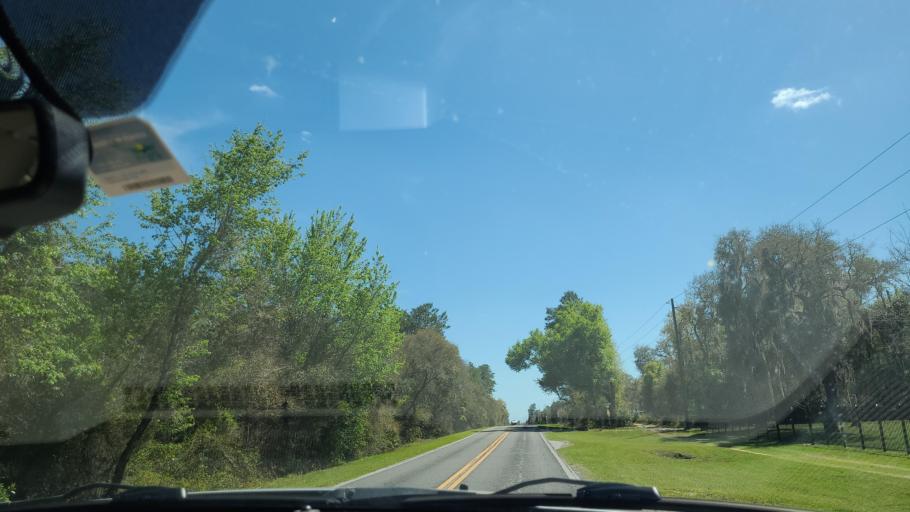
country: US
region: Florida
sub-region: Marion County
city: Citra
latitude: 29.4262
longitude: -81.9148
